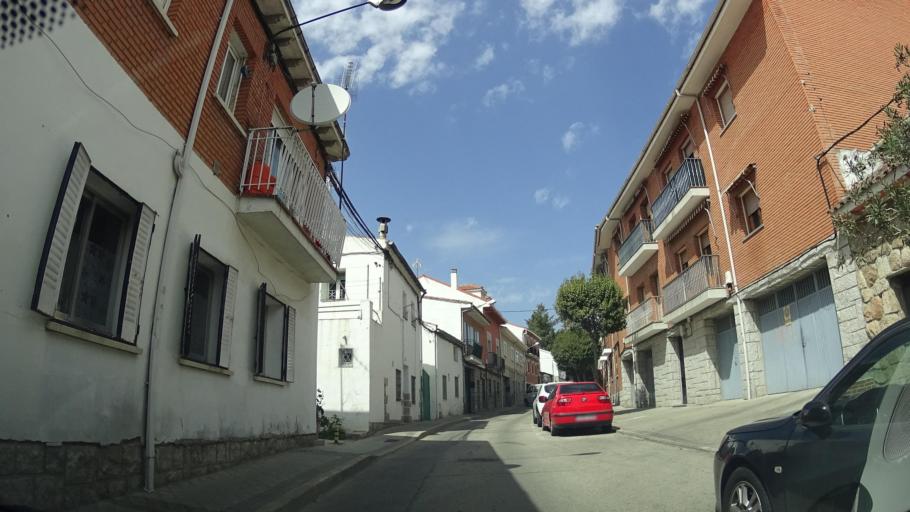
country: ES
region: Madrid
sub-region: Provincia de Madrid
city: Colmenar Viejo
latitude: 40.6634
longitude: -3.7707
